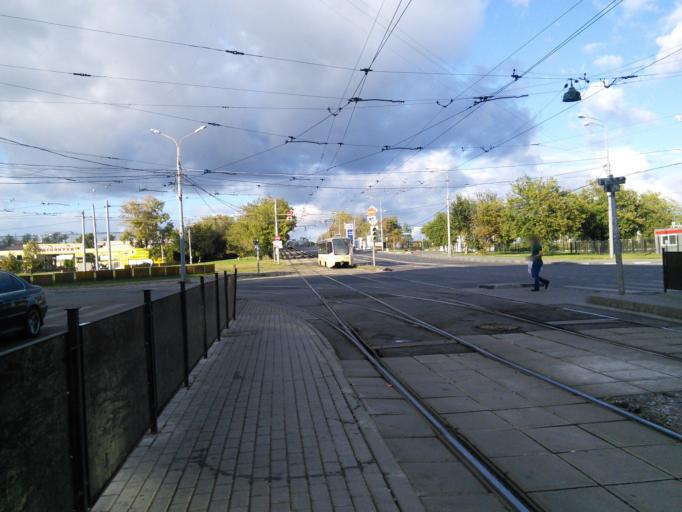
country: RU
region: Moskovskaya
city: Bogorodskoye
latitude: 55.8132
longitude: 37.7353
